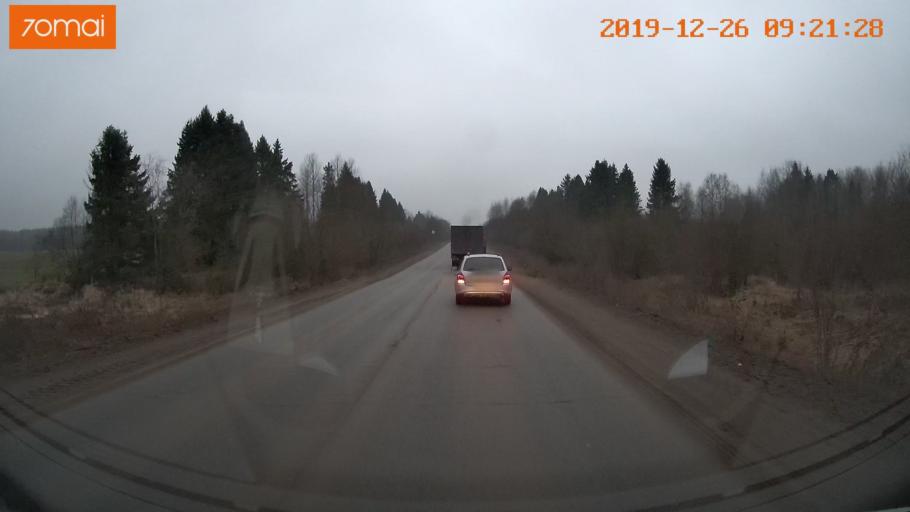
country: RU
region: Vologda
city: Gryazovets
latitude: 58.9704
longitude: 40.2243
